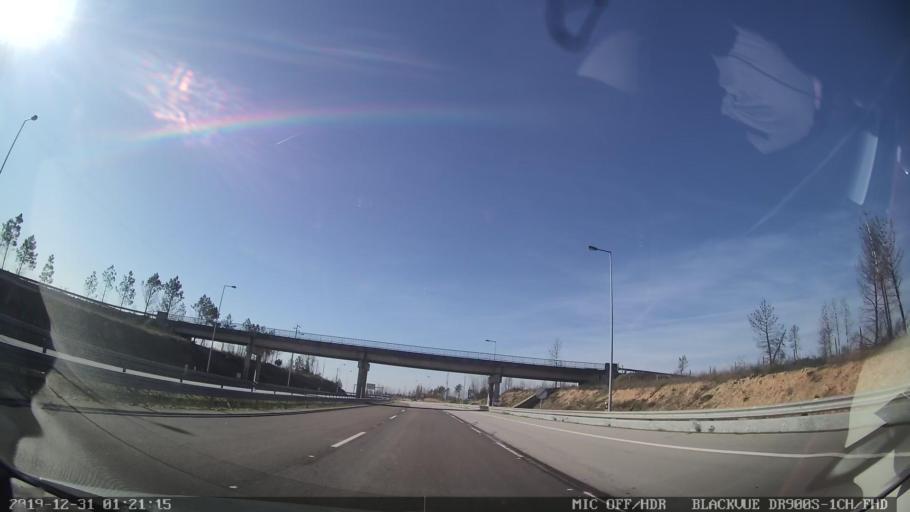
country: PT
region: Santarem
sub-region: Macao
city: Macao
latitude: 39.5301
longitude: -7.9519
